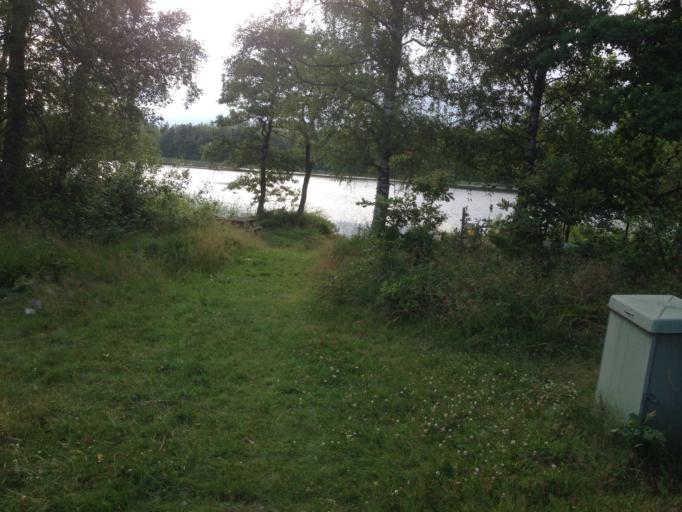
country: SE
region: Kronoberg
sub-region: Ljungby Kommun
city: Ljungby
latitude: 56.8687
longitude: 13.7787
